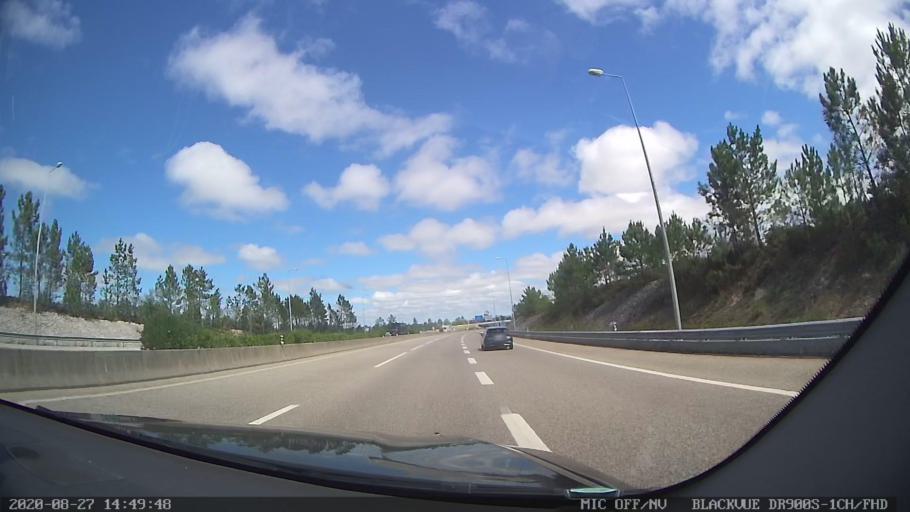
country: PT
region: Leiria
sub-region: Marinha Grande
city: Marinha Grande
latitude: 39.7417
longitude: -8.8777
